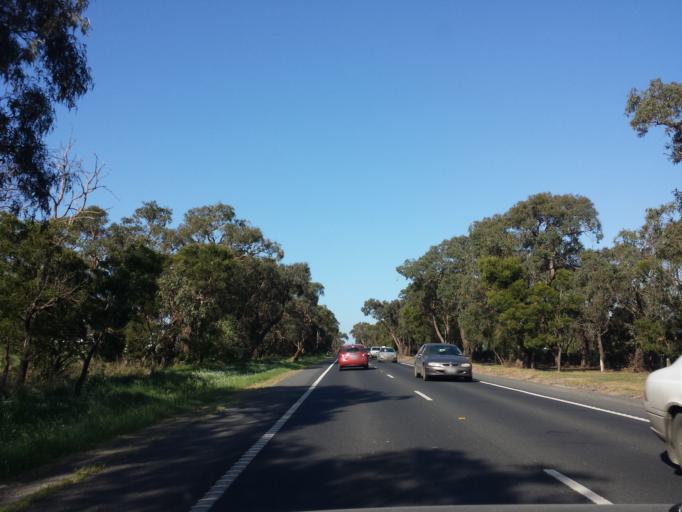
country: AU
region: Victoria
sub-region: Casey
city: Narre Warren North
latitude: -37.9659
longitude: 145.3224
